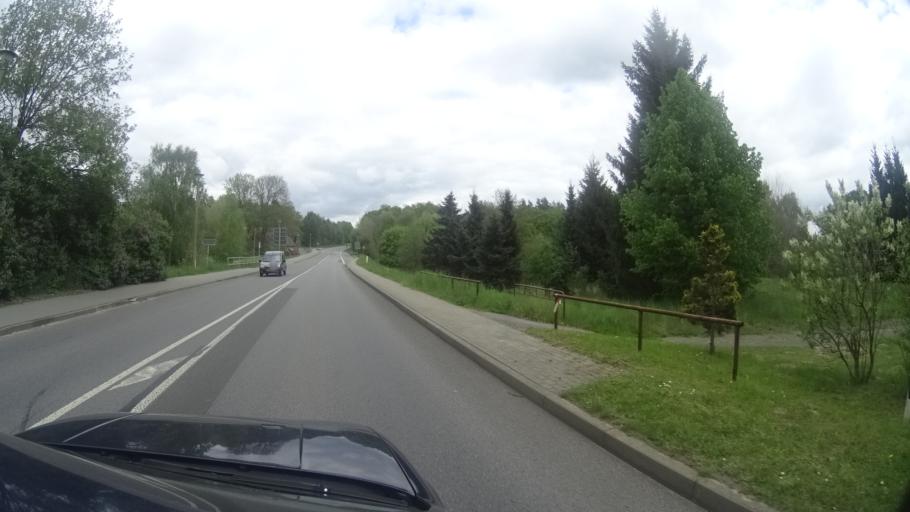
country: DE
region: Mecklenburg-Vorpommern
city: Malchow
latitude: 53.4641
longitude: 12.4257
